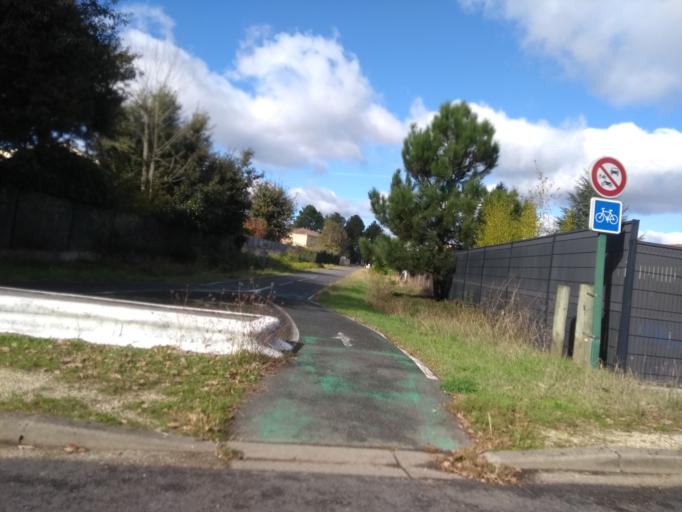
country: FR
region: Aquitaine
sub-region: Departement de la Gironde
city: Saint-Aubin-de-Medoc
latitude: 44.7922
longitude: -0.7026
